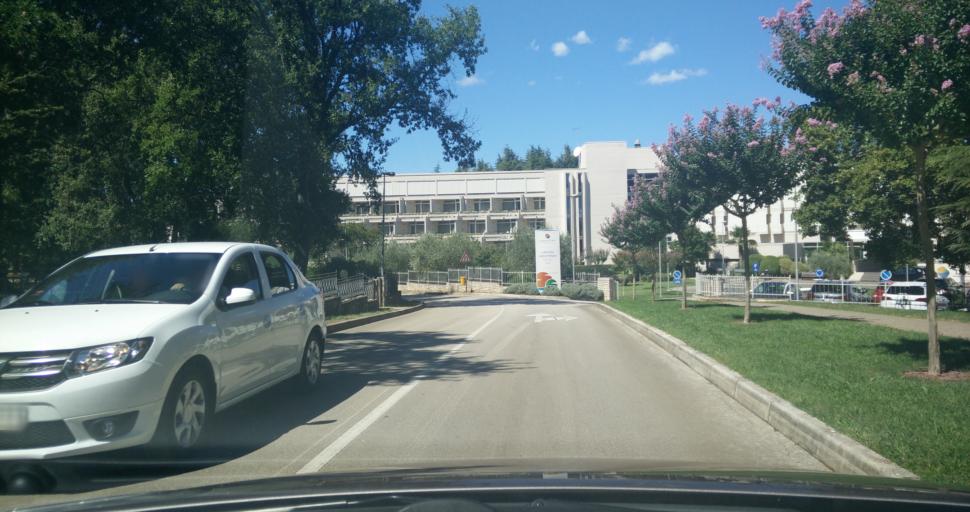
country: HR
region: Istarska
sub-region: Grad Porec
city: Porec
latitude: 45.2117
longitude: 13.5965
